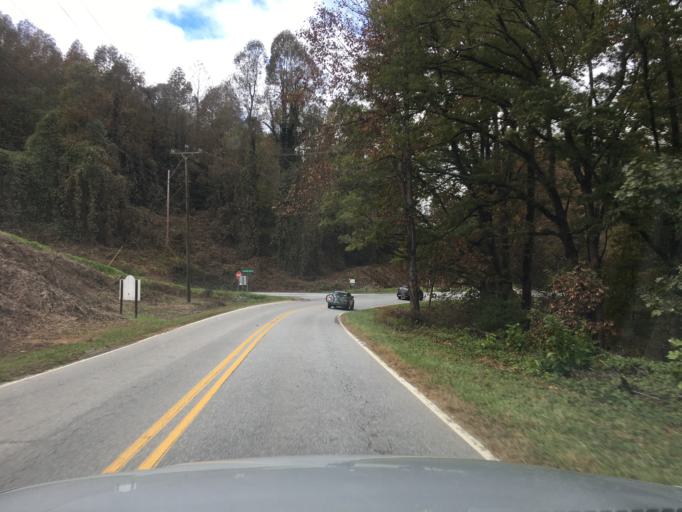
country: US
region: North Carolina
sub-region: Henderson County
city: Flat Rock
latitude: 35.2485
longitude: -82.4260
